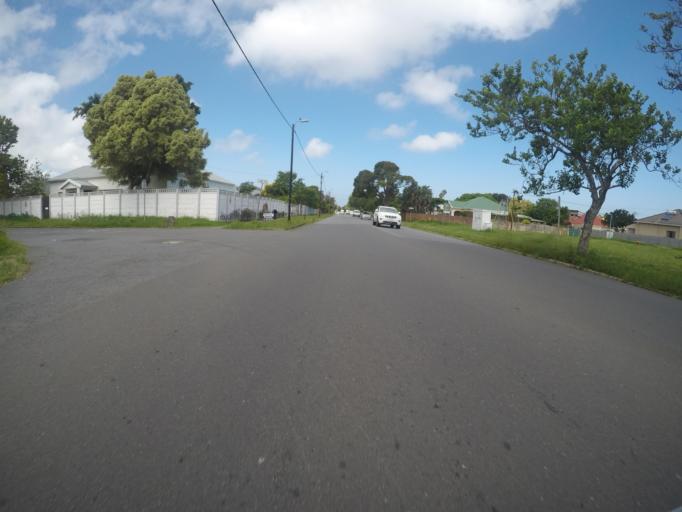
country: ZA
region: Eastern Cape
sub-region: Buffalo City Metropolitan Municipality
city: East London
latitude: -32.9790
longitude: 27.9086
